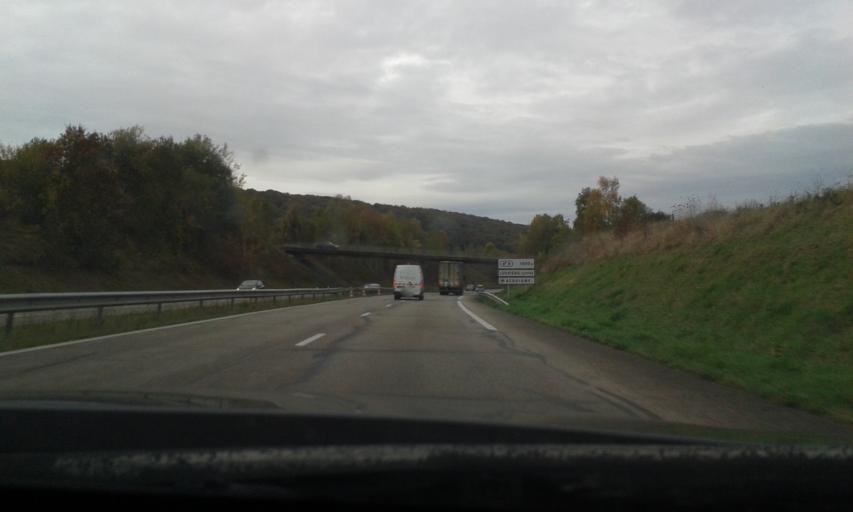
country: FR
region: Haute-Normandie
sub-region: Departement de l'Eure
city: Acquigny
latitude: 49.1692
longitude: 1.1720
